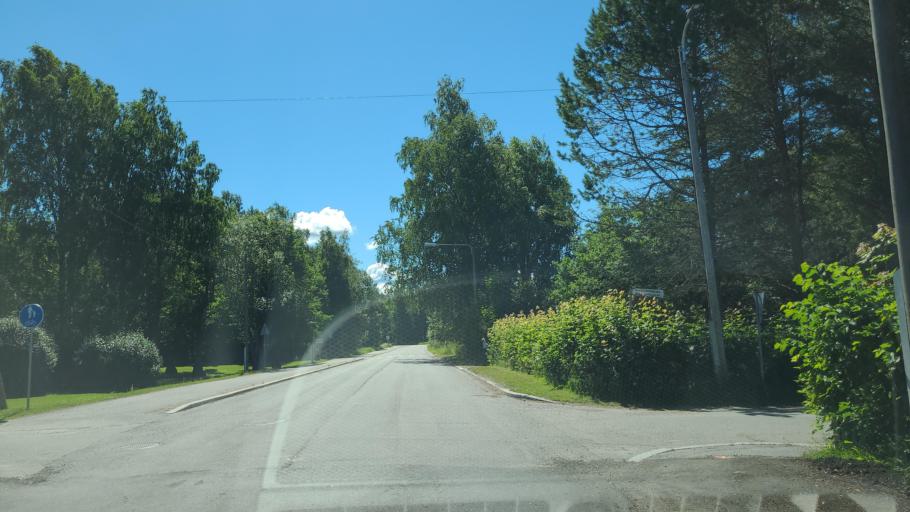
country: FI
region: Ostrobothnia
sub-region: Vaasa
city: Ristinummi
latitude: 63.0706
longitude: 21.7235
